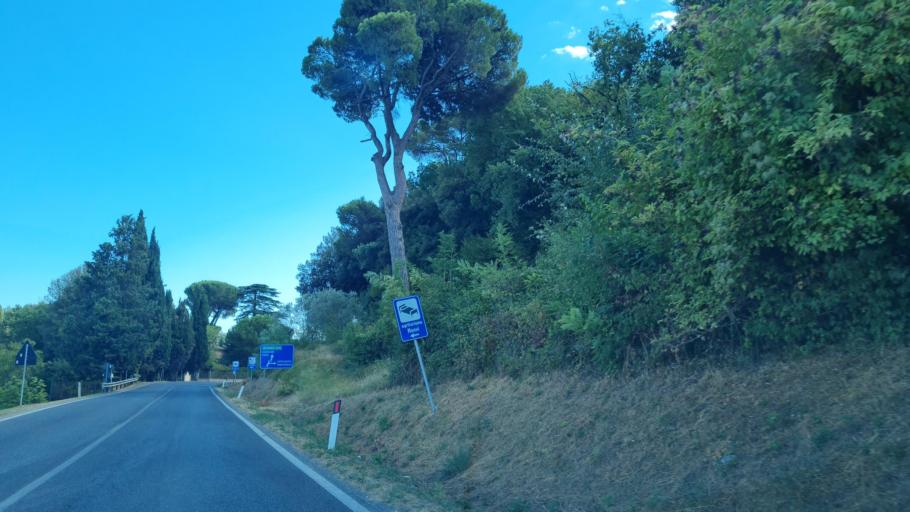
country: IT
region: Tuscany
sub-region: Provincia di Siena
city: Sant'Albino
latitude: 43.0760
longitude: 11.7858
